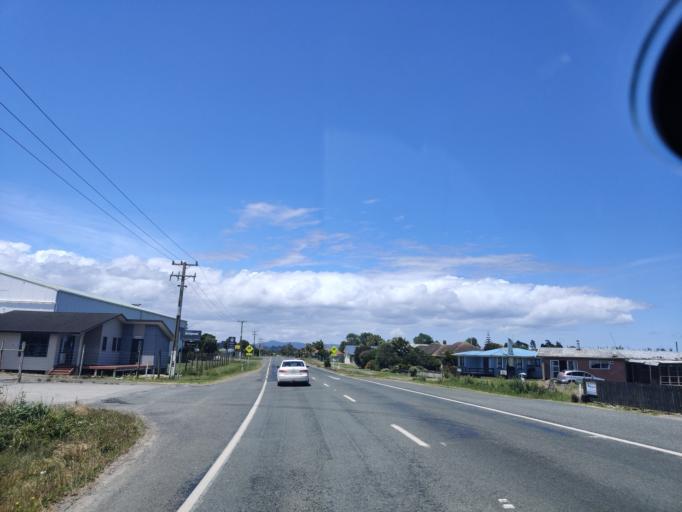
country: NZ
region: Northland
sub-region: Far North District
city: Kaitaia
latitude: -35.0377
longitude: 173.2547
